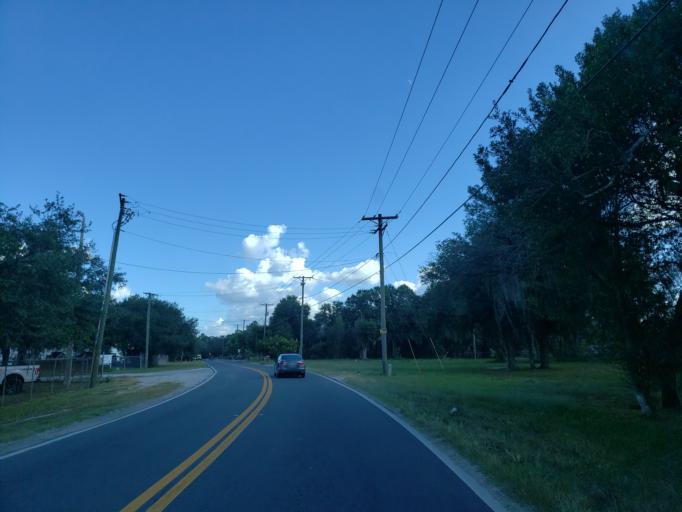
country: US
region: Florida
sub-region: Hillsborough County
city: Dover
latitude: 28.0047
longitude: -82.1700
